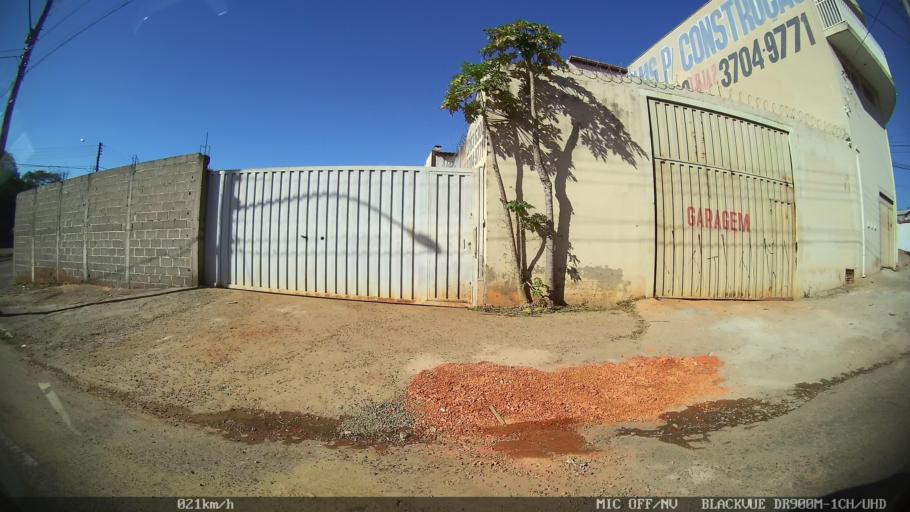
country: BR
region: Sao Paulo
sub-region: Franca
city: Franca
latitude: -20.4901
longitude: -47.4285
